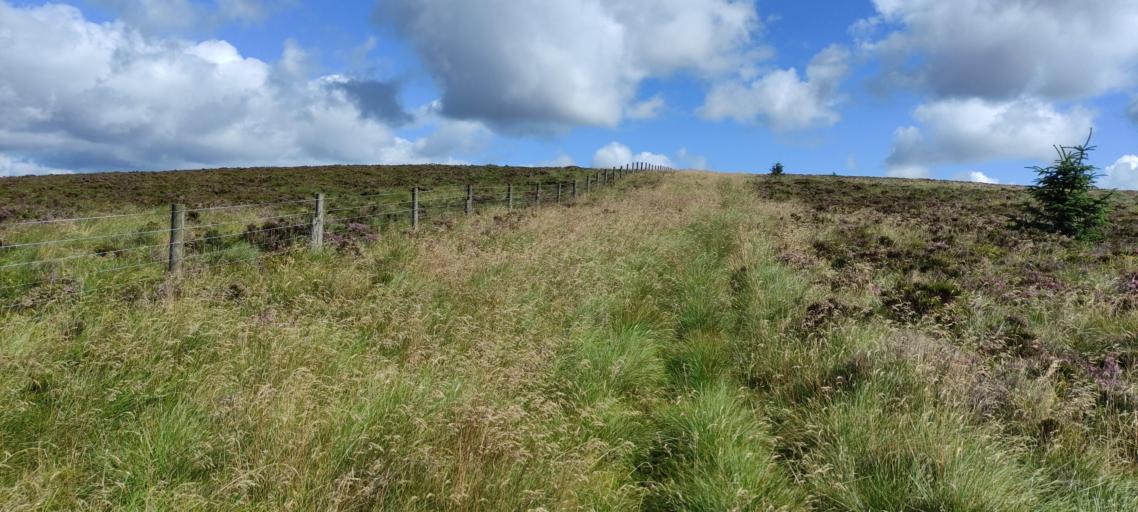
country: GB
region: Scotland
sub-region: Dumfries and Galloway
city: Langholm
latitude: 55.2367
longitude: -3.0396
